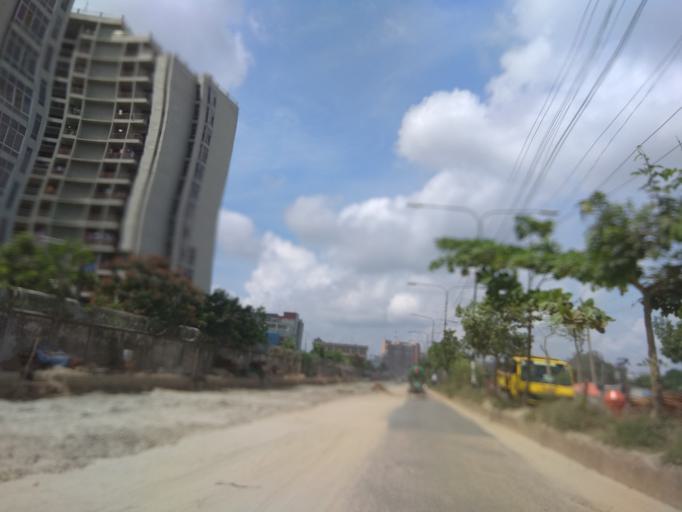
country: BD
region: Dhaka
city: Paltan
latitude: 23.8099
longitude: 90.3916
